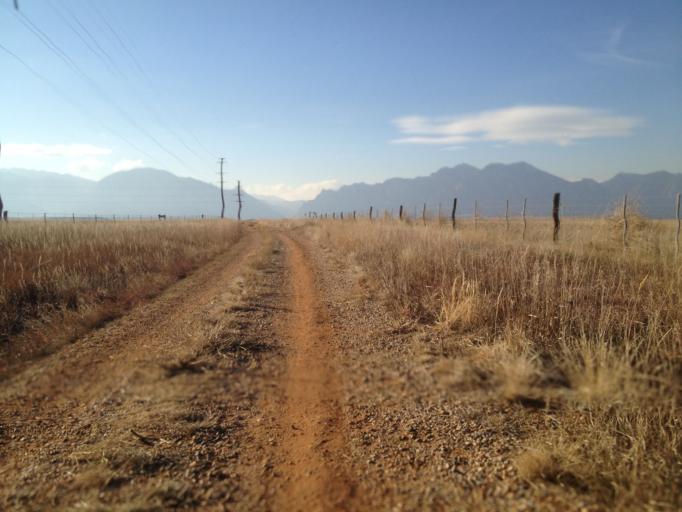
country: US
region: Colorado
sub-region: Boulder County
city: Superior
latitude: 39.9287
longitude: -105.1906
